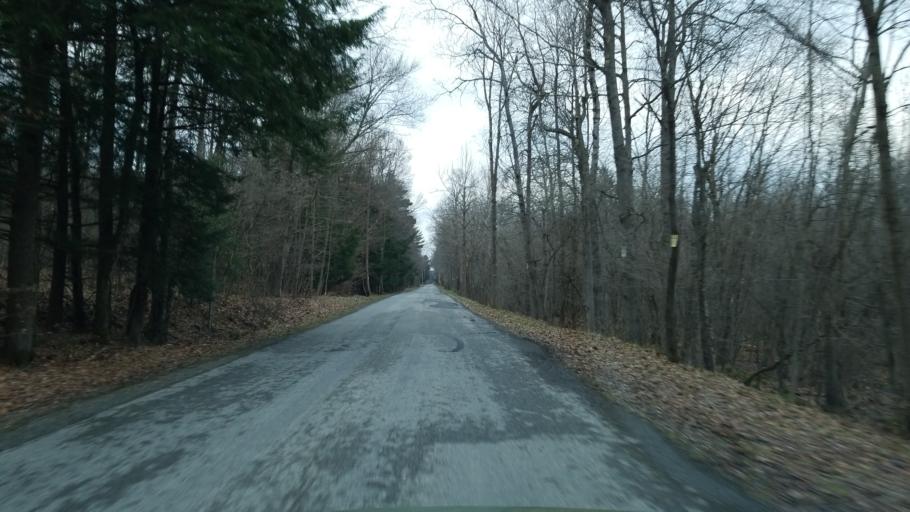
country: US
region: Pennsylvania
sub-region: Jefferson County
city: Falls Creek
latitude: 41.1799
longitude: -78.7950
